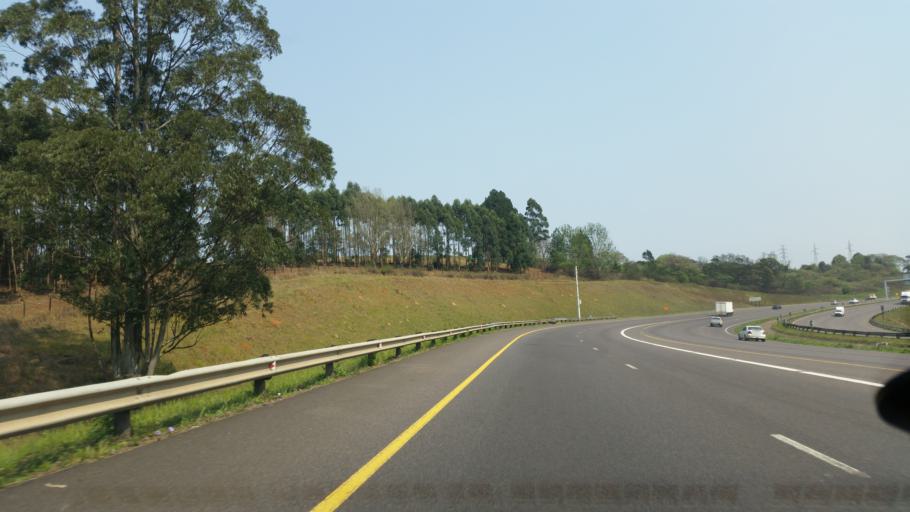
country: ZA
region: KwaZulu-Natal
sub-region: eThekwini Metropolitan Municipality
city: Mpumalanga
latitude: -29.7878
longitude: 30.7213
